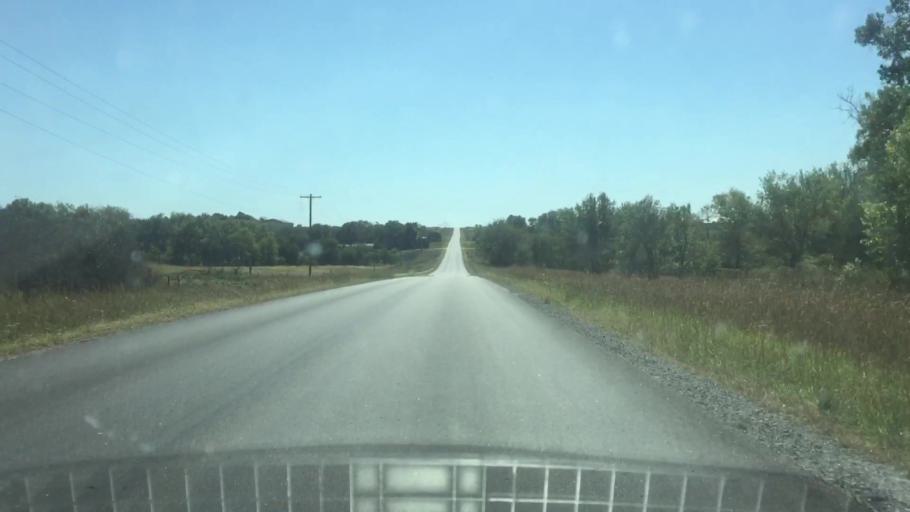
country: US
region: Kansas
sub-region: Marshall County
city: Marysville
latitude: 39.9329
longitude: -96.6009
